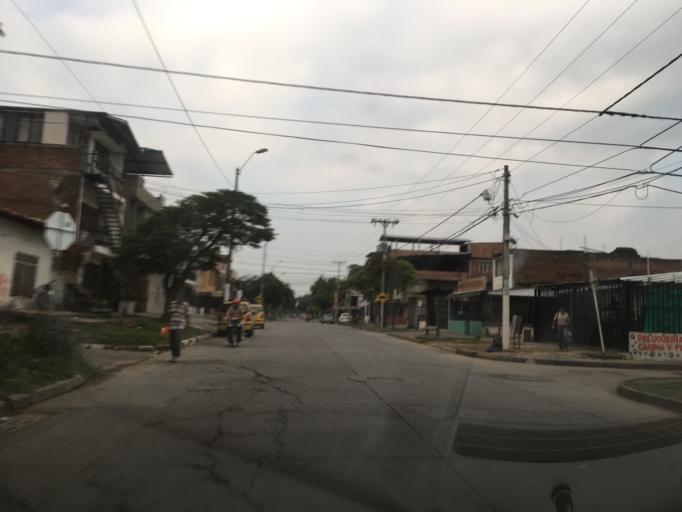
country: CO
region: Valle del Cauca
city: Cali
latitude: 3.4179
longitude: -76.5221
